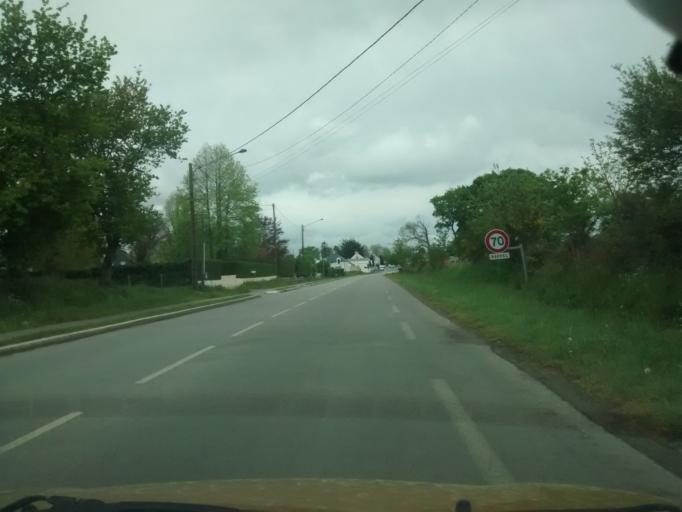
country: FR
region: Brittany
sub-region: Departement du Morbihan
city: Questembert
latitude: 47.6768
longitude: -2.4503
